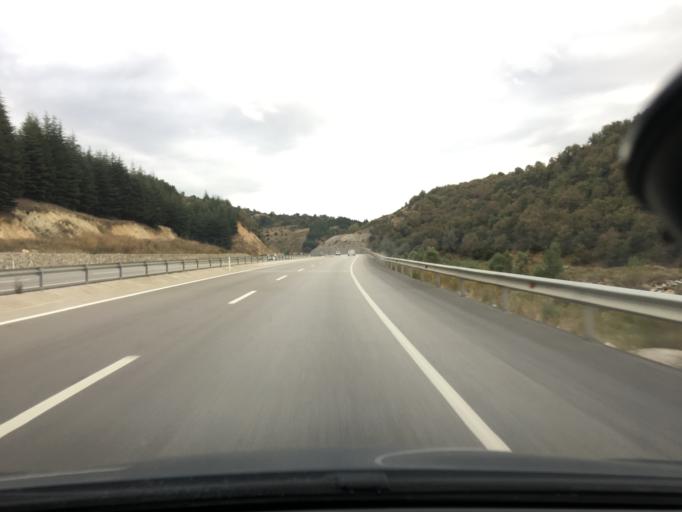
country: TR
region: Afyonkarahisar
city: Sincanli
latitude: 38.7019
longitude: 30.3198
